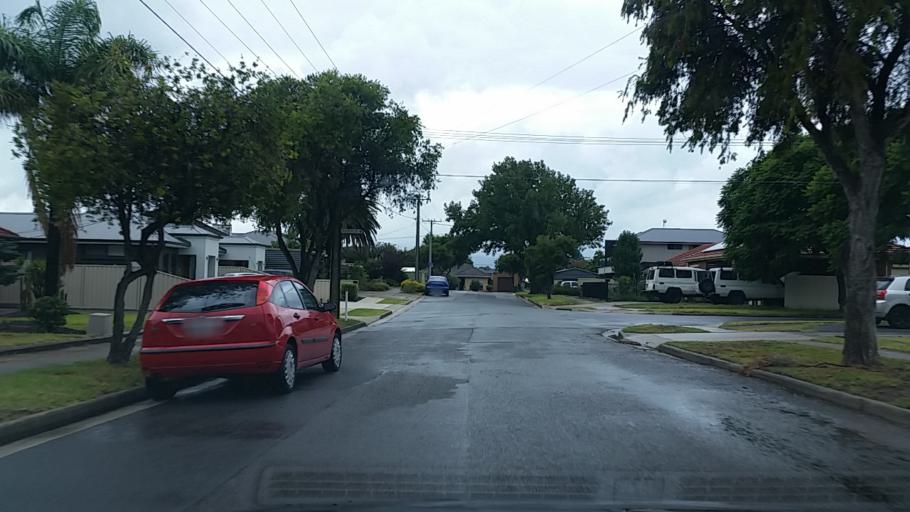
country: AU
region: South Australia
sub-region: Charles Sturt
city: Seaton
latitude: -34.9015
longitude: 138.5219
